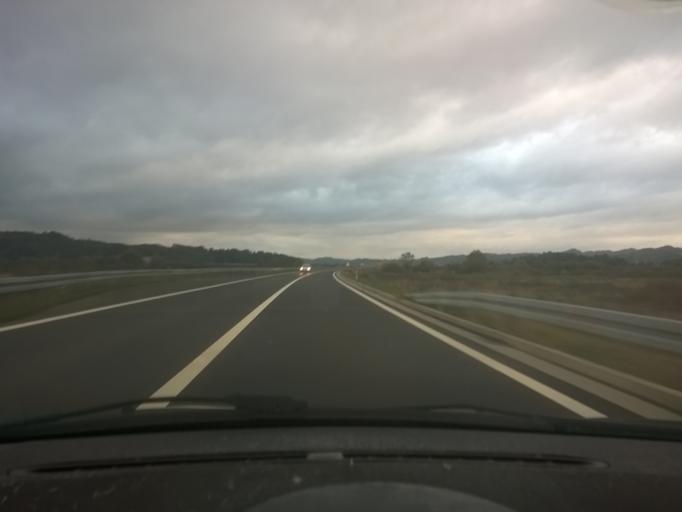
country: HR
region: Krapinsko-Zagorska
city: Zabok
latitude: 46.0143
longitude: 15.9195
